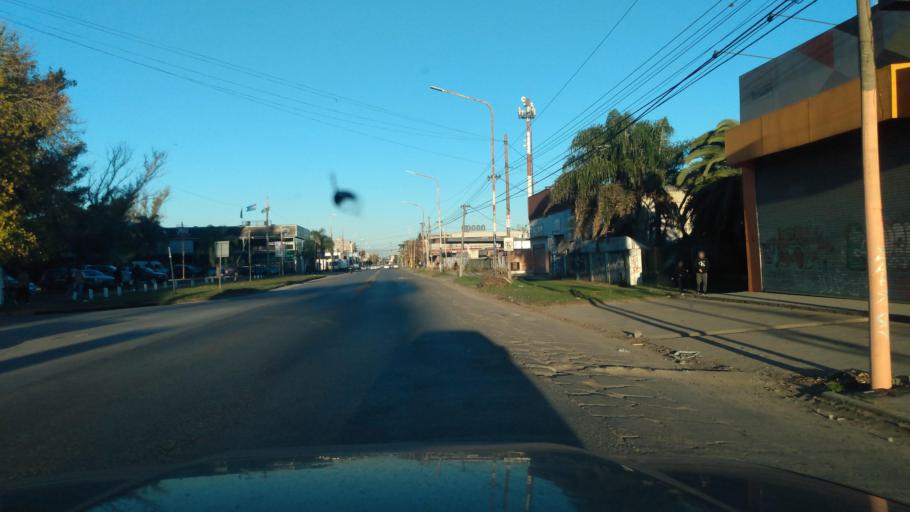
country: AR
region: Buenos Aires
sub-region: Partido de Merlo
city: Merlo
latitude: -34.6544
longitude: -58.7709
